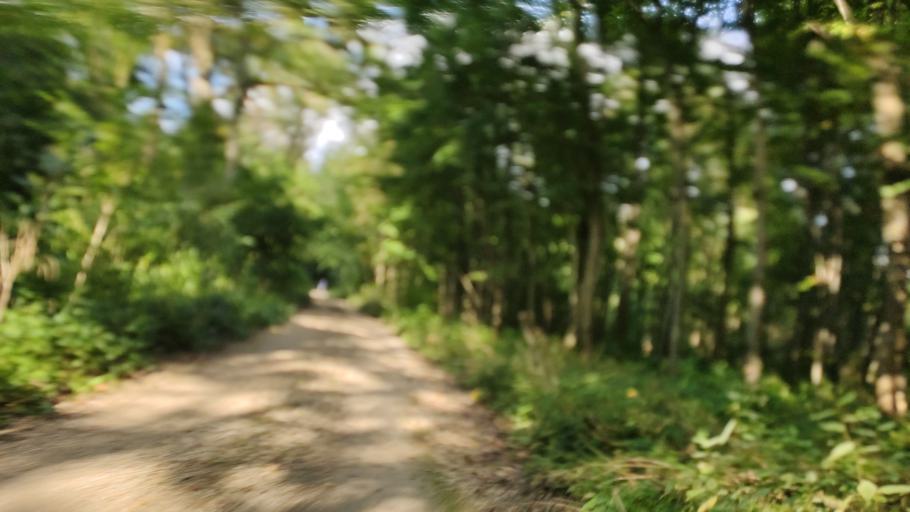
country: DE
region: Bavaria
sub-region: Swabia
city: Klosterlechfeld
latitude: 48.1356
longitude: 10.8631
